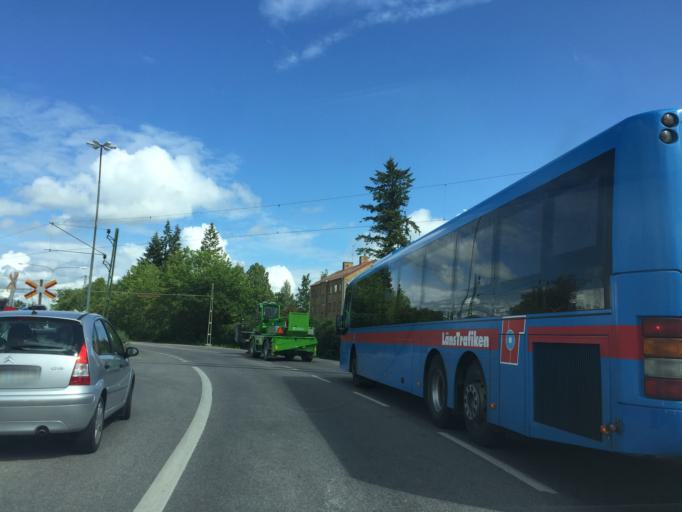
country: SE
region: OErebro
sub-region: Orebro Kommun
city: Orebro
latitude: 59.2795
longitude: 15.2150
